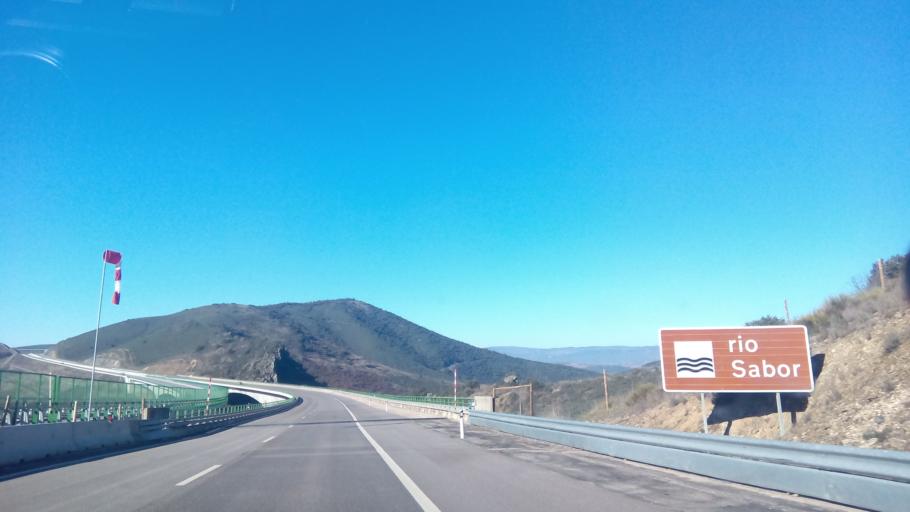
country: PT
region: Braganca
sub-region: Braganca Municipality
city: Braganca
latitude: 41.7739
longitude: -6.6741
